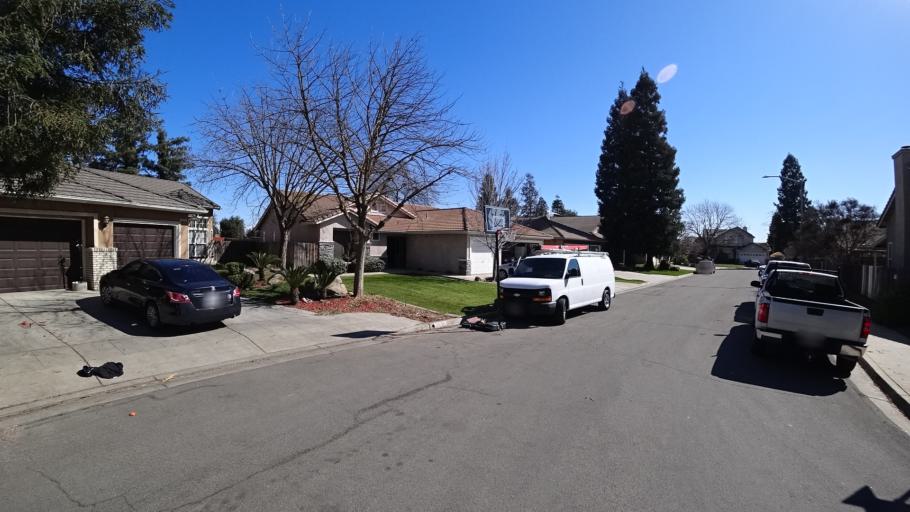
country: US
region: California
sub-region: Fresno County
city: Clovis
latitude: 36.8627
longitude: -119.7415
